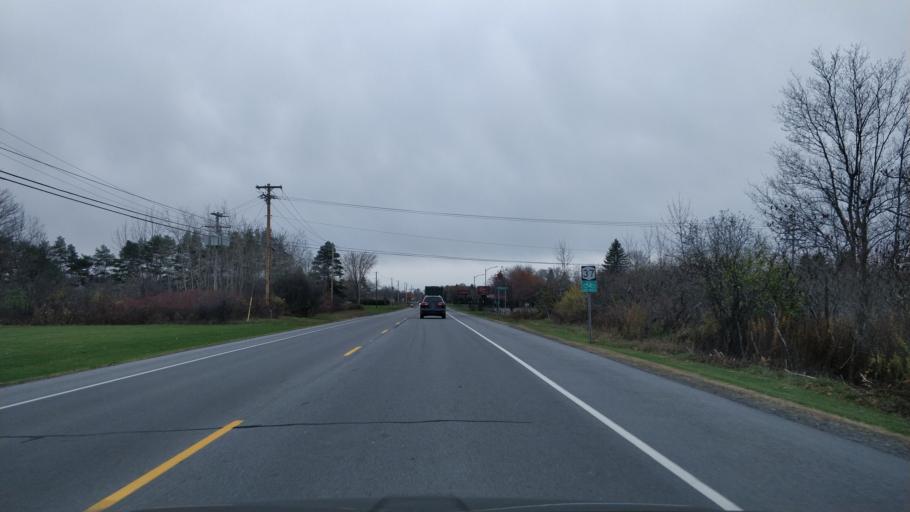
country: CA
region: Ontario
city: Prescott
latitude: 44.6667
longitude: -75.5366
